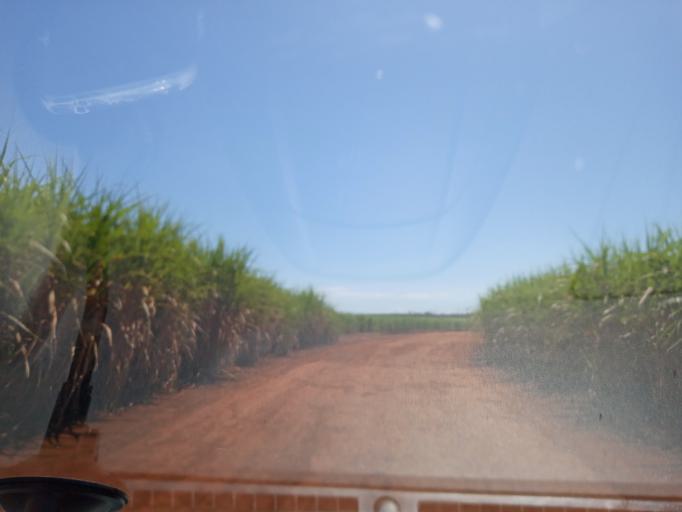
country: BR
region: Goias
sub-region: Itumbiara
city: Itumbiara
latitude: -18.4427
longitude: -49.1495
